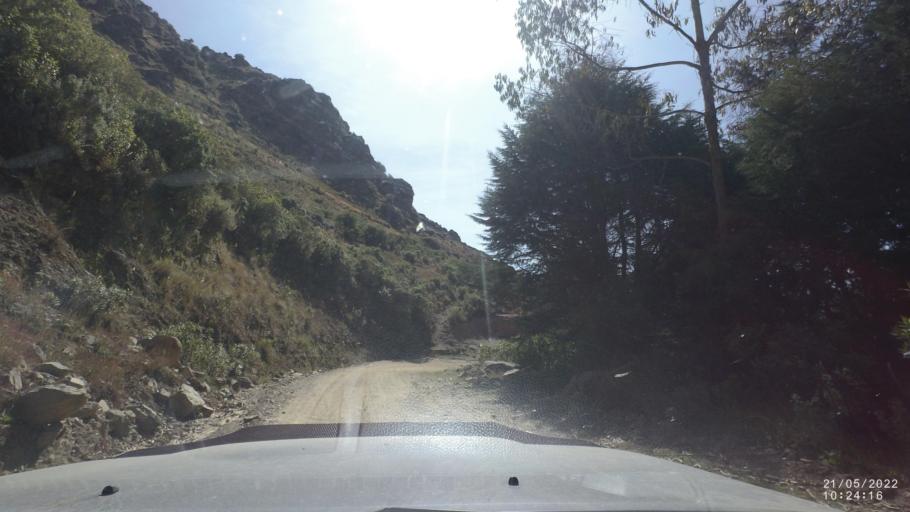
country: BO
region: Cochabamba
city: Colomi
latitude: -17.3232
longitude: -65.9482
